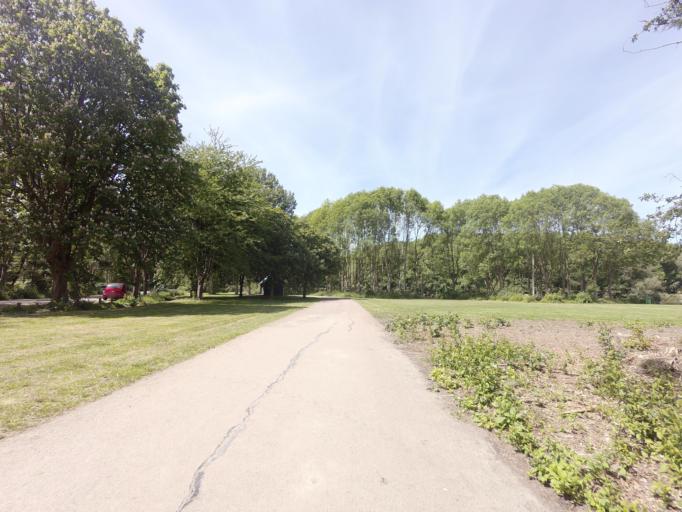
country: NL
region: North Holland
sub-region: Gemeente Zaanstad
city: Zaanstad
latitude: 52.3934
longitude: 4.7420
